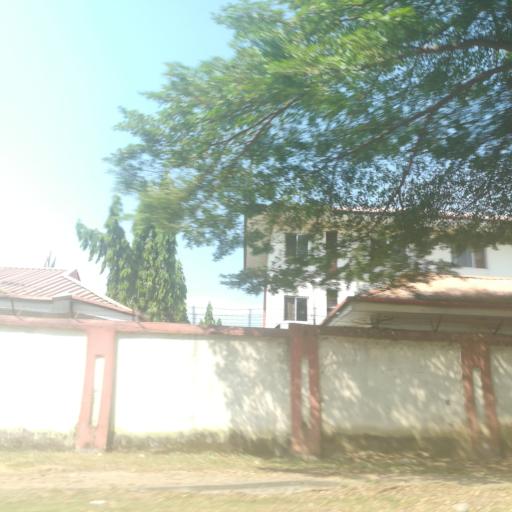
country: NG
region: Abuja Federal Capital Territory
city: Abuja
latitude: 9.0686
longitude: 7.4391
